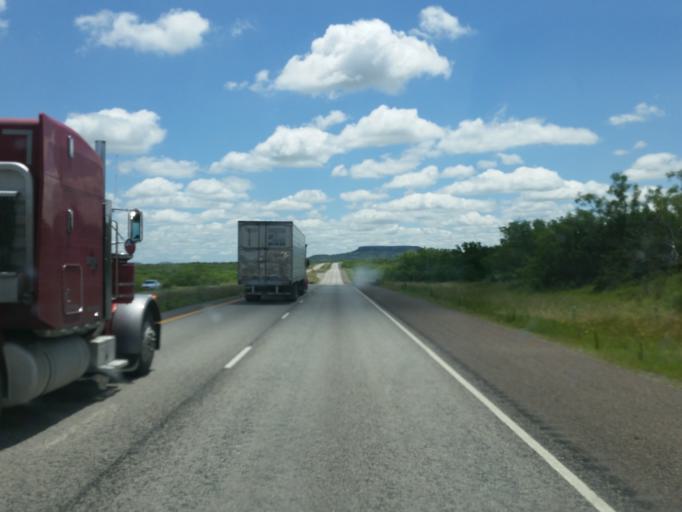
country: US
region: Texas
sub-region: Garza County
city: Post
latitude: 32.9835
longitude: -101.1210
